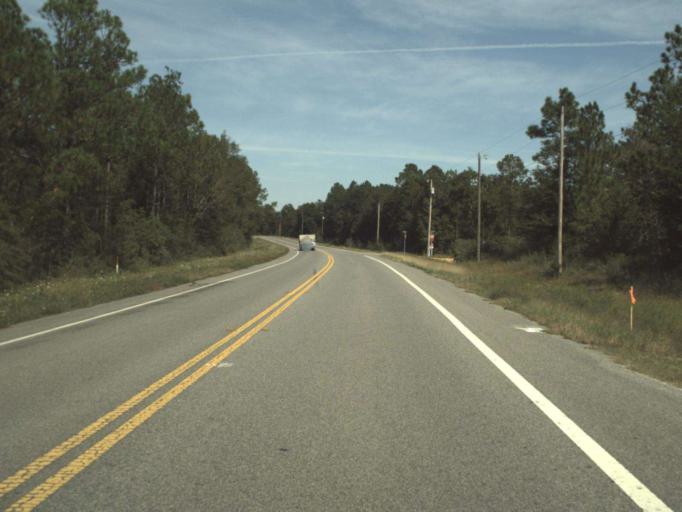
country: US
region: Florida
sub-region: Washington County
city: Chipley
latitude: 30.5873
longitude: -85.5919
